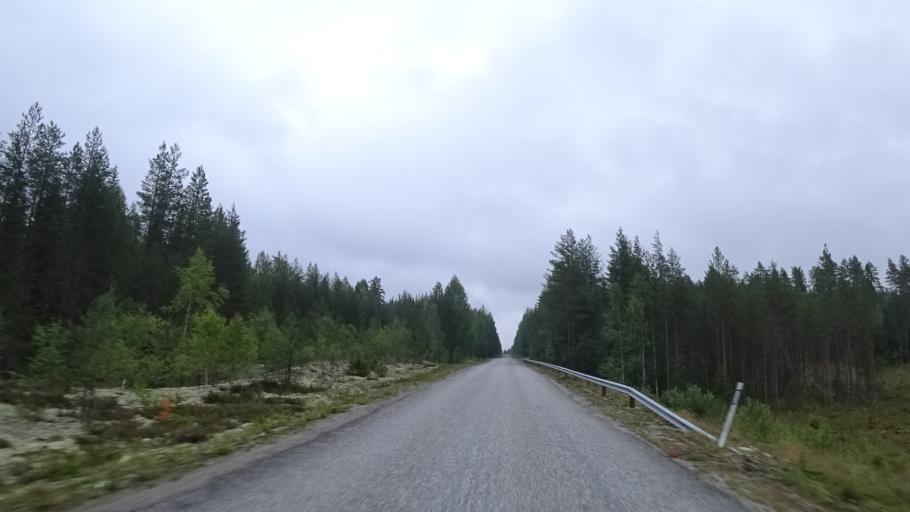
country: FI
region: North Karelia
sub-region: Joensuu
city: Ilomantsi
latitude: 63.2287
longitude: 30.8150
